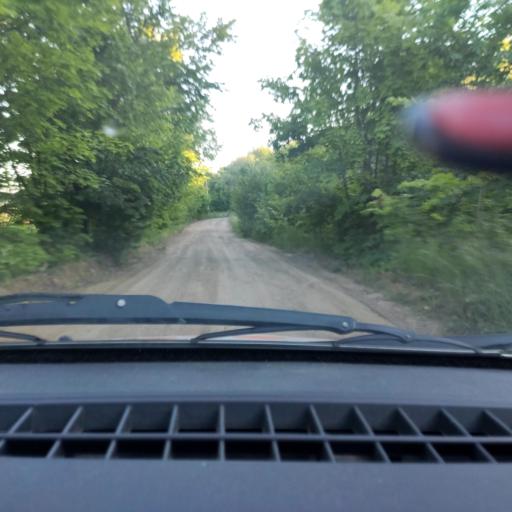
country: RU
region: Bashkortostan
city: Karmaskaly
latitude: 54.3716
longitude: 55.9108
